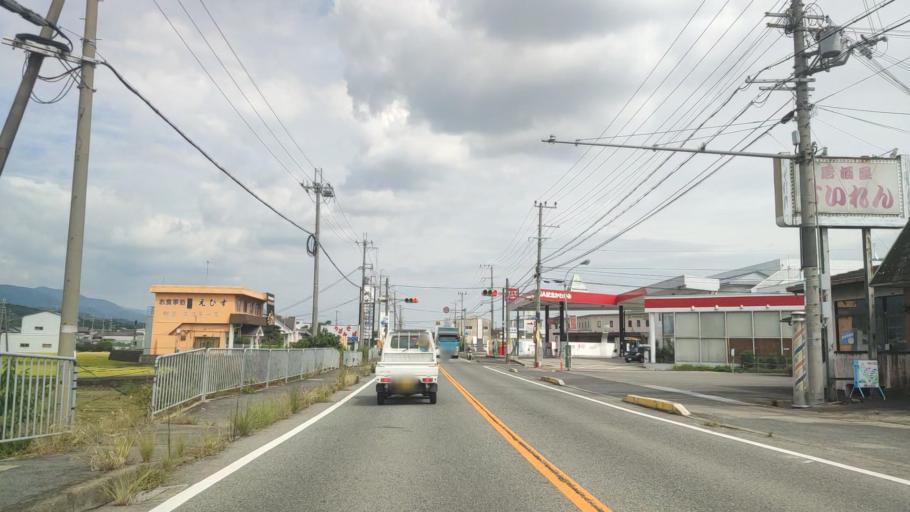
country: JP
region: Wakayama
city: Hashimoto
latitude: 34.2927
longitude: 135.4918
